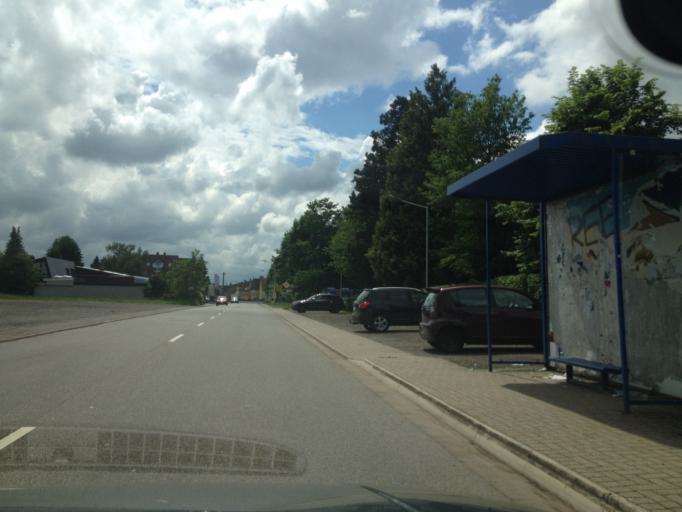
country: DE
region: Saarland
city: Bexbach
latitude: 49.3423
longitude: 7.2619
